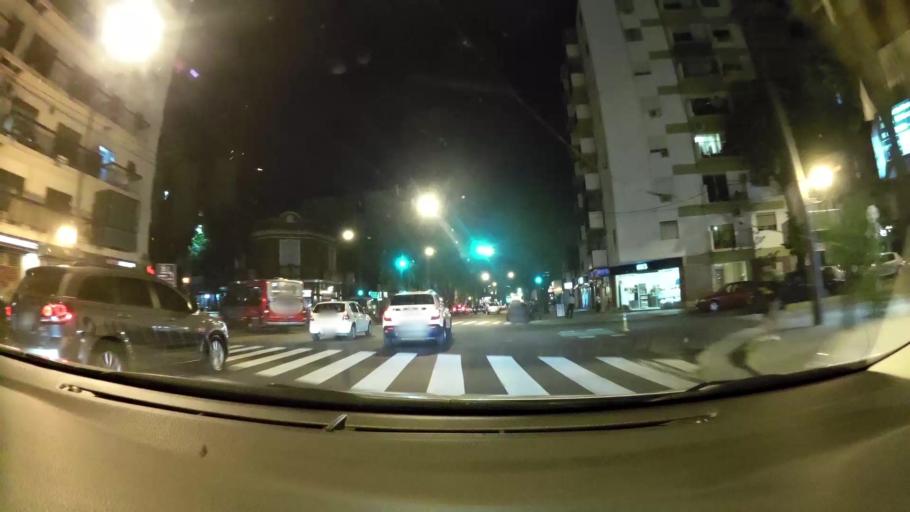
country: AR
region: Buenos Aires F.D.
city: Colegiales
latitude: -34.5744
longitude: -58.4599
